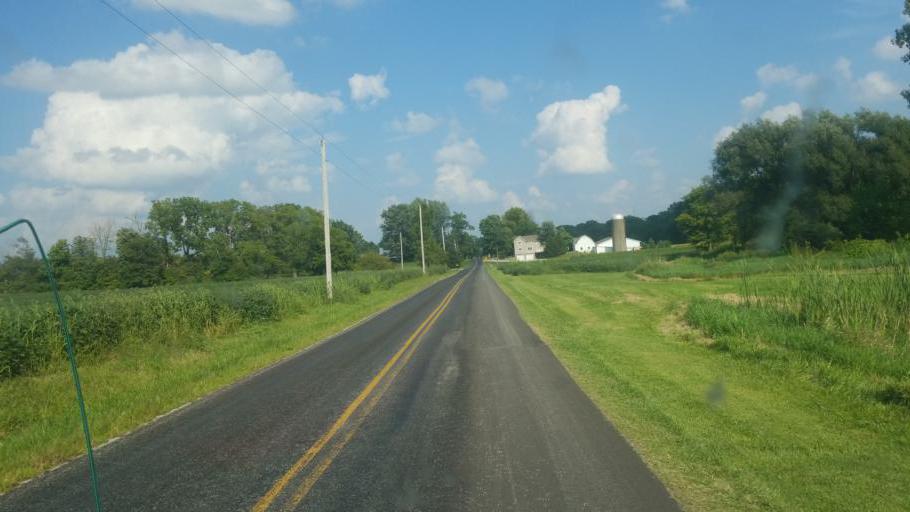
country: US
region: Ohio
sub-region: Medina County
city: Lodi
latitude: 40.9937
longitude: -82.0516
